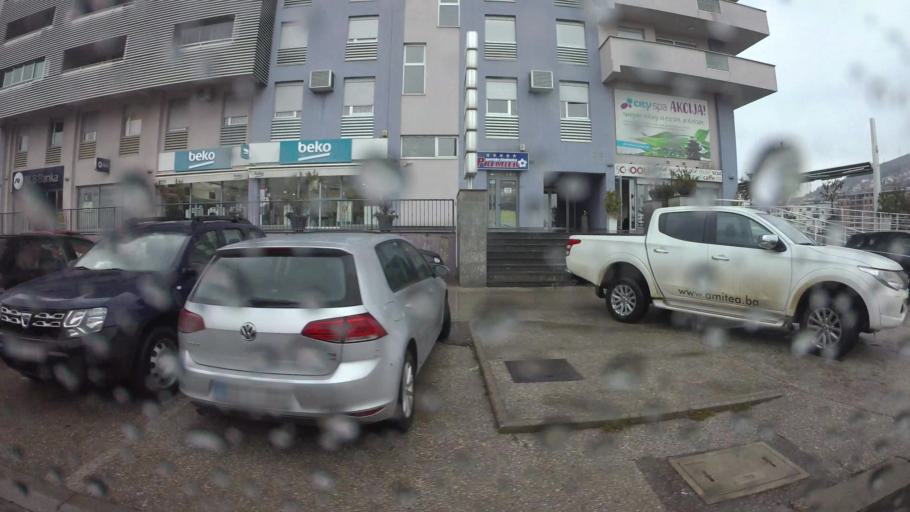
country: BA
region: Federation of Bosnia and Herzegovina
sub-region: Hercegovacko-Bosanski Kanton
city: Mostar
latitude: 43.3482
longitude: 17.8096
